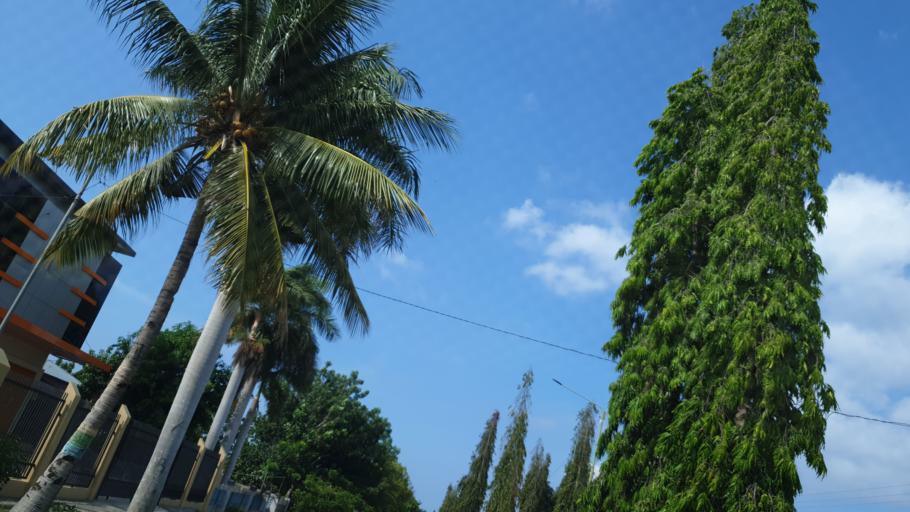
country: ID
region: East Nusa Tenggara
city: Waioti
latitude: -8.6312
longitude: 122.2365
